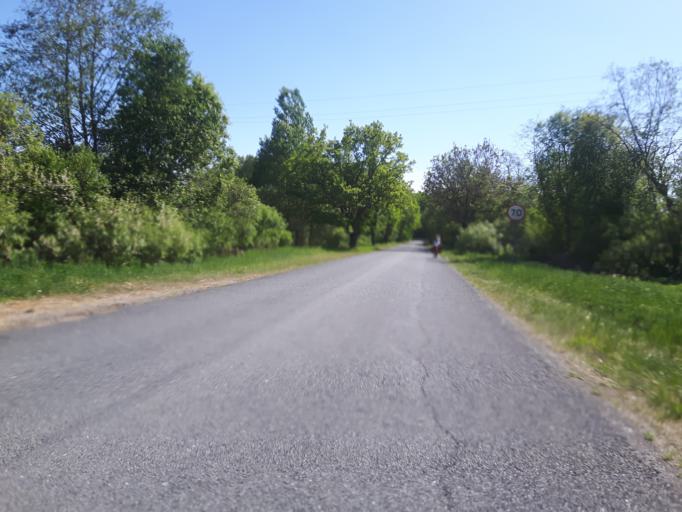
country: EE
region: Laeaene-Virumaa
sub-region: Haljala vald
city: Haljala
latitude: 59.5430
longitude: 26.2364
